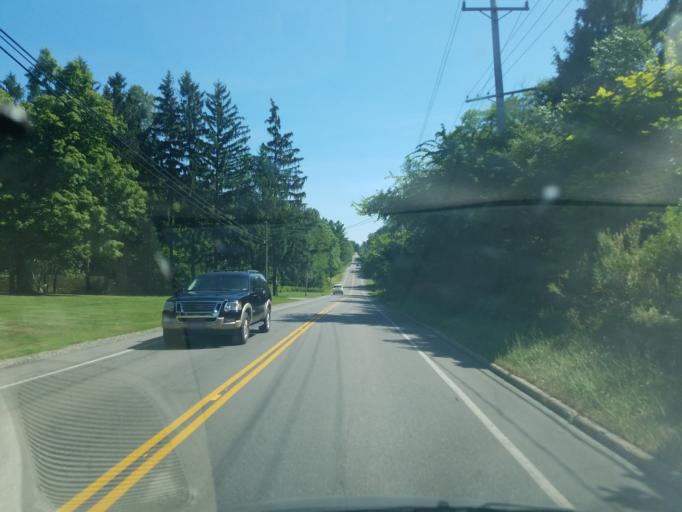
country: US
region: Ohio
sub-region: Geauga County
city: Burton
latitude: 41.4952
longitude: -81.1452
